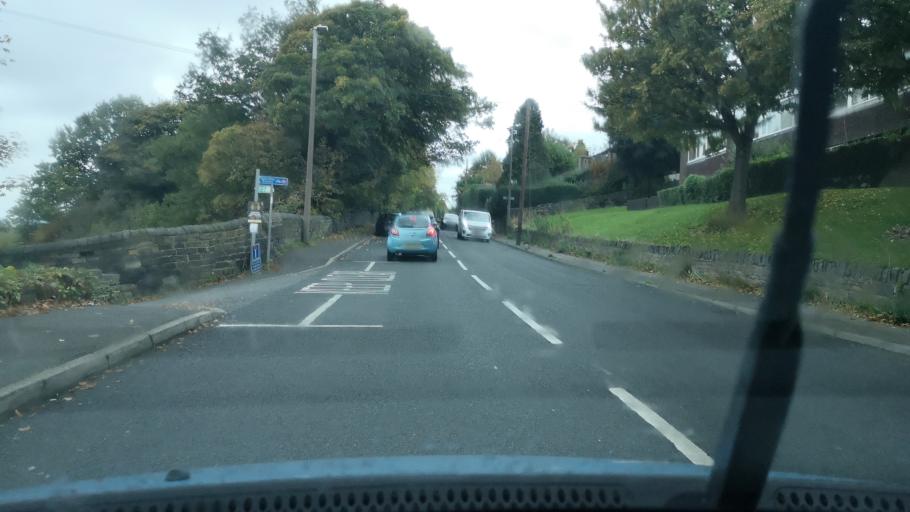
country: GB
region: England
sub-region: Kirklees
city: Heckmondwike
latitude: 53.6964
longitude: -1.6590
